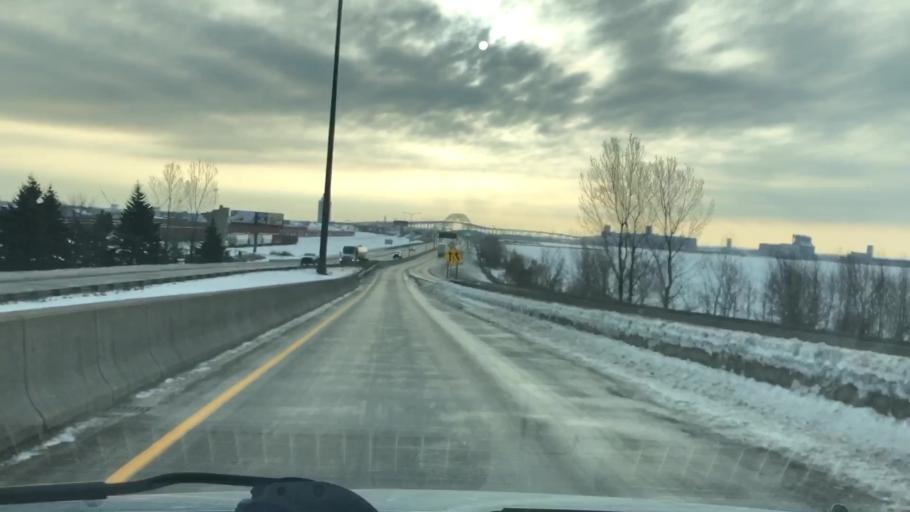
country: US
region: Minnesota
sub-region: Saint Louis County
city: Duluth
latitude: 46.7652
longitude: -92.1199
